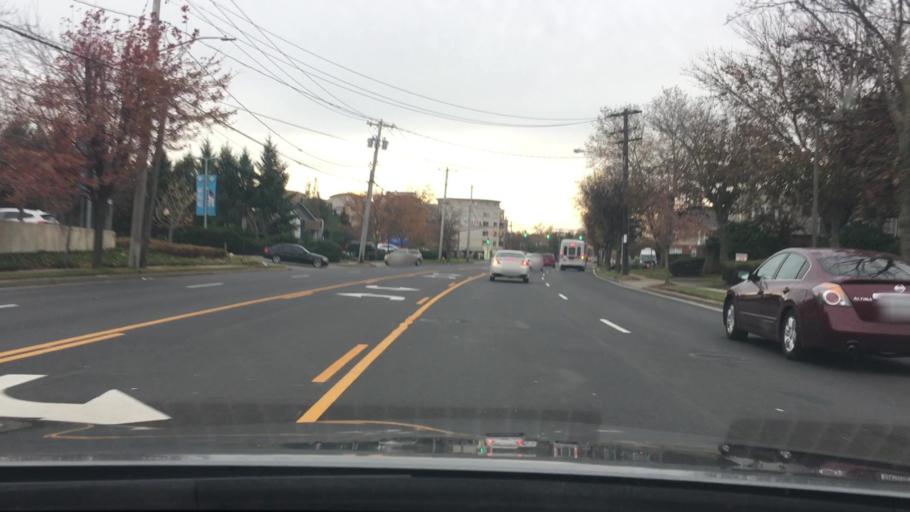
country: US
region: New York
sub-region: Nassau County
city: New Cassel
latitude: 40.7789
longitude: -73.5588
